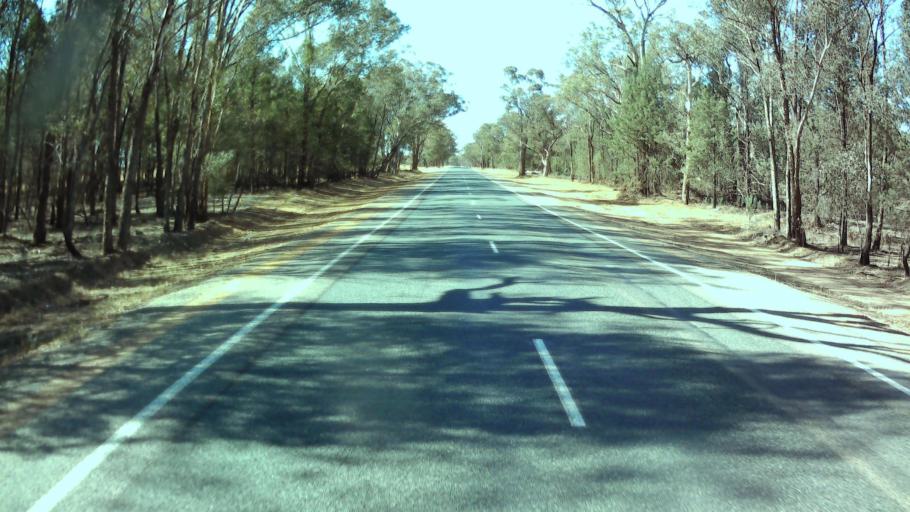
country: AU
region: New South Wales
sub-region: Weddin
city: Grenfell
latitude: -33.7417
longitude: 148.0887
